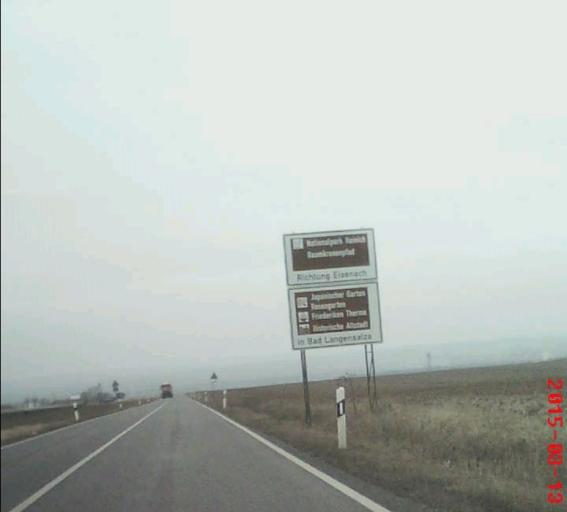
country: DE
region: Thuringia
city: Bad Langensalza
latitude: 51.0827
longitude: 10.6404
